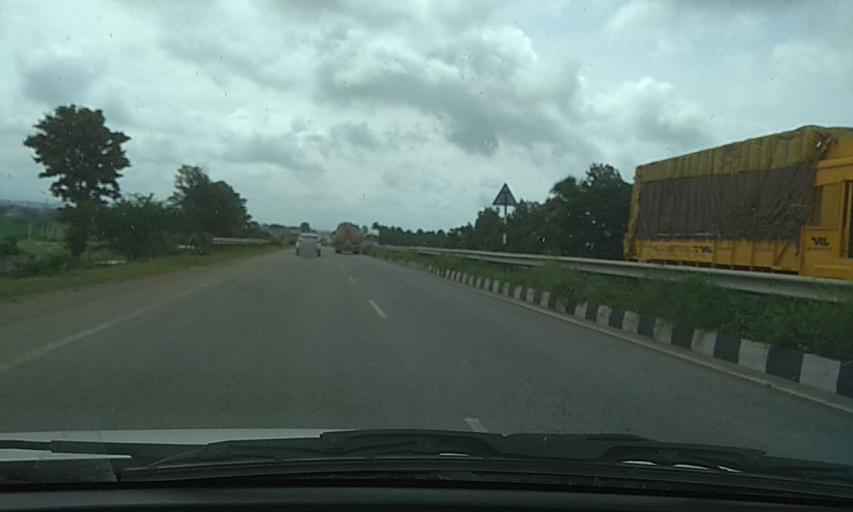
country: IN
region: Karnataka
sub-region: Davanagere
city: Harihar
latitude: 14.4592
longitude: 75.8586
